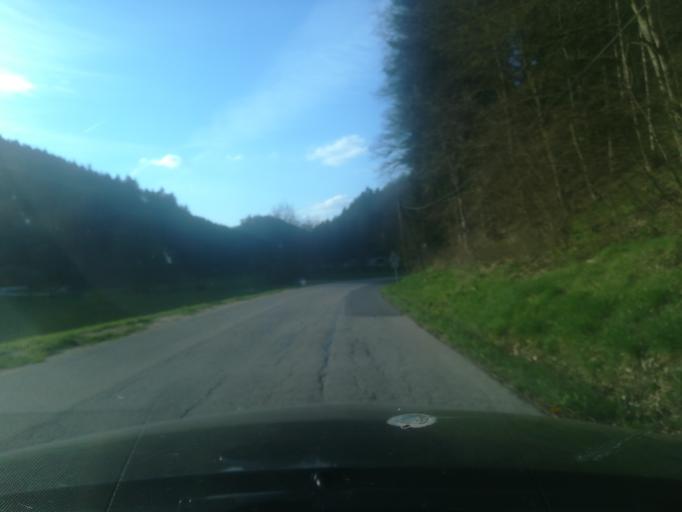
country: AT
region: Upper Austria
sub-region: Politischer Bezirk Perg
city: Bad Kreuzen
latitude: 48.2753
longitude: 14.7873
